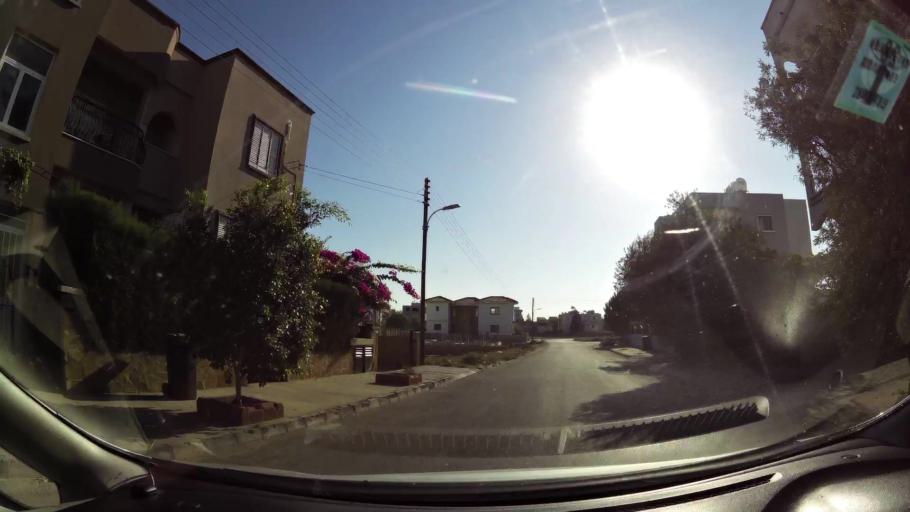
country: CY
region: Lefkosia
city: Nicosia
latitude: 35.2110
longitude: 33.3000
